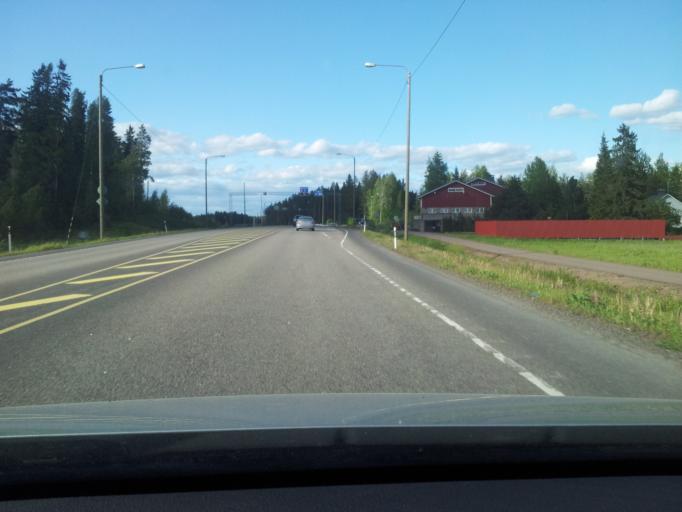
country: FI
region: Kymenlaakso
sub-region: Kouvola
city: Elimaeki
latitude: 60.8250
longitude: 26.5355
